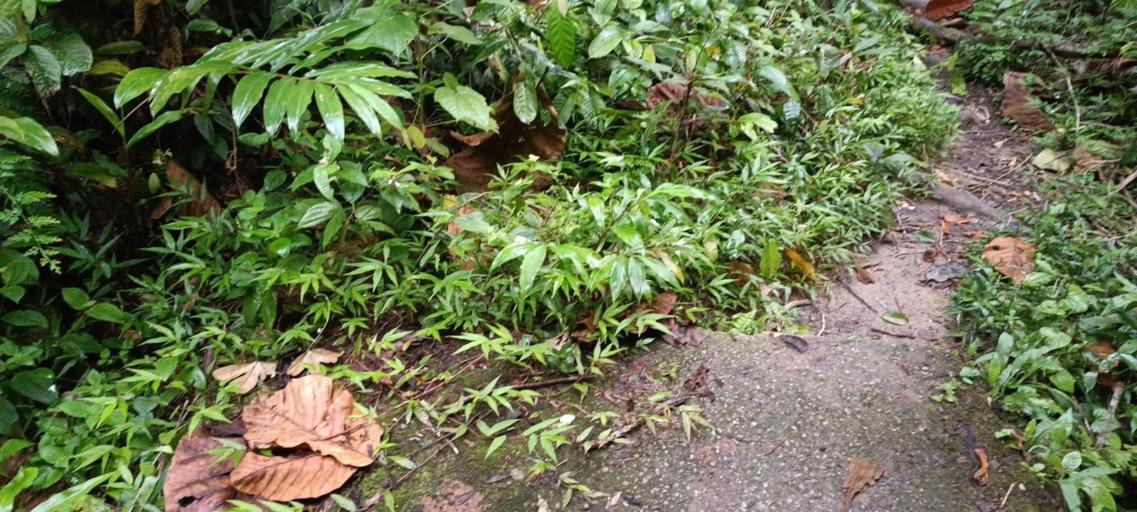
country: MY
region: Penang
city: Bukit Mertajam
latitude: 5.3576
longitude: 100.4908
